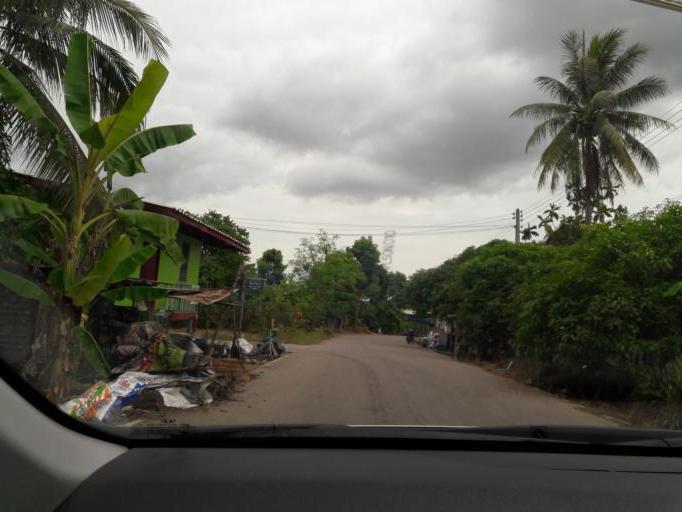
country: TH
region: Ratchaburi
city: Damnoen Saduak
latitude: 13.5552
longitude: 99.9905
